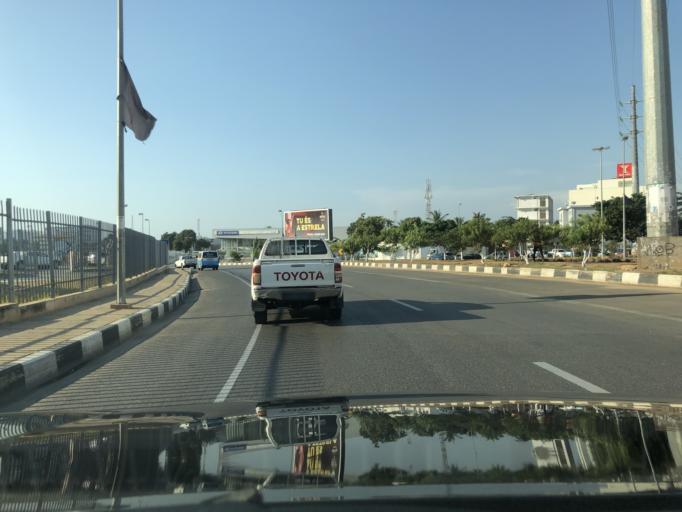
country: AO
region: Luanda
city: Luanda
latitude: -8.8948
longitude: 13.1815
